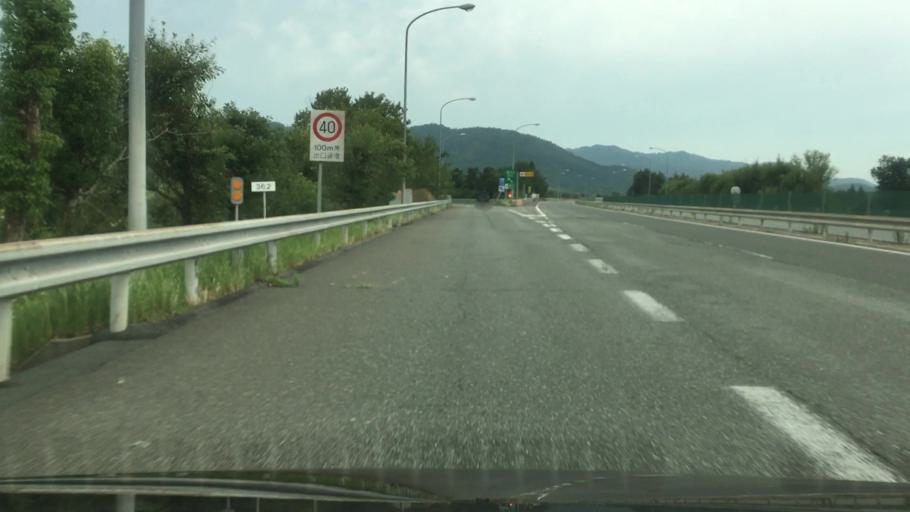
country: JP
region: Hyogo
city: Sasayama
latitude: 35.1622
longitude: 135.1192
